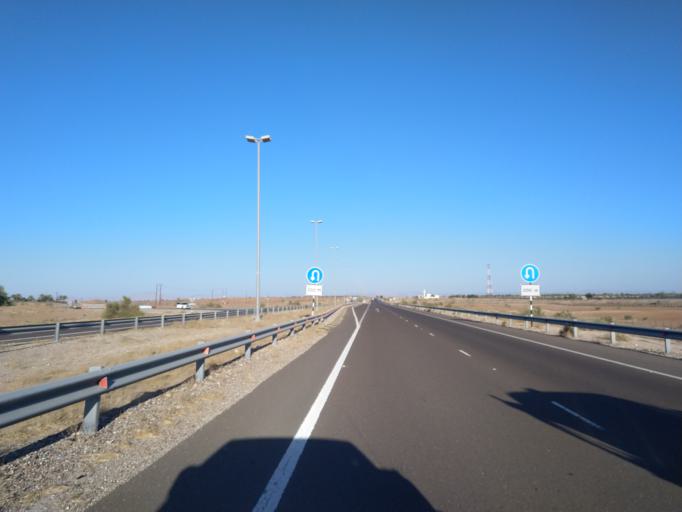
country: OM
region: Al Buraimi
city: Al Buraymi
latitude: 24.5406
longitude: 55.6231
